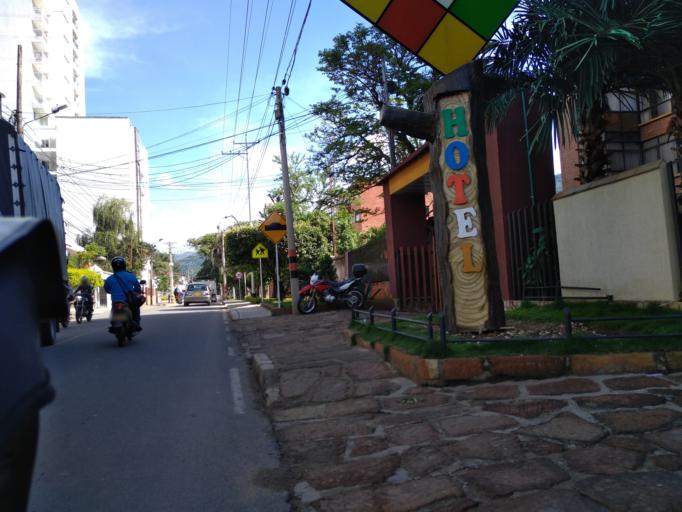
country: CO
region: Santander
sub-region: San Gil
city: San Gil
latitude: 6.5499
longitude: -73.1305
